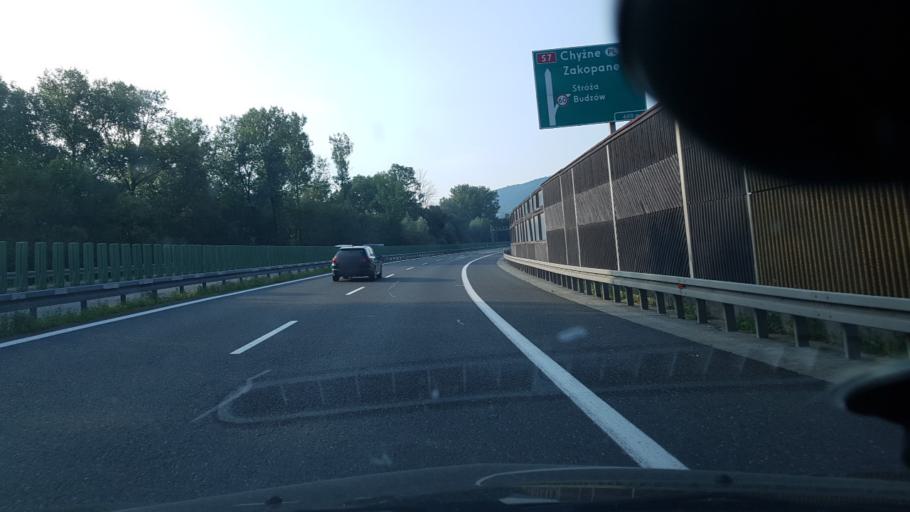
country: PL
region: Lesser Poland Voivodeship
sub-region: Powiat myslenicki
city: Stroza
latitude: 49.8066
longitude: 19.9248
